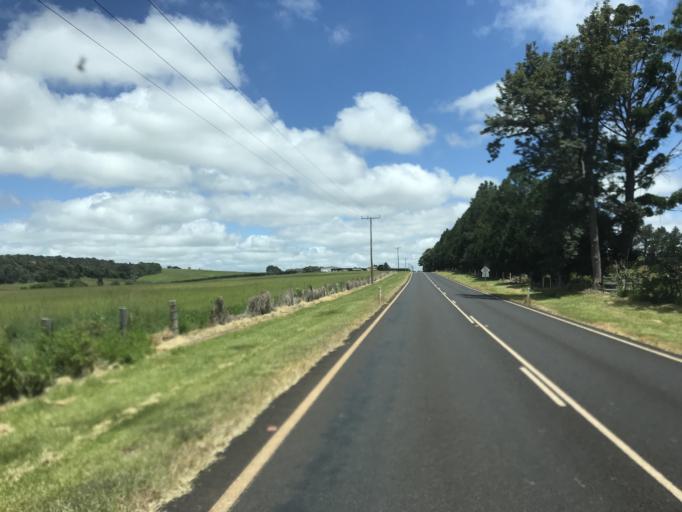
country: AU
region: Queensland
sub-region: Tablelands
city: Ravenshoe
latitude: -17.5077
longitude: 145.4596
